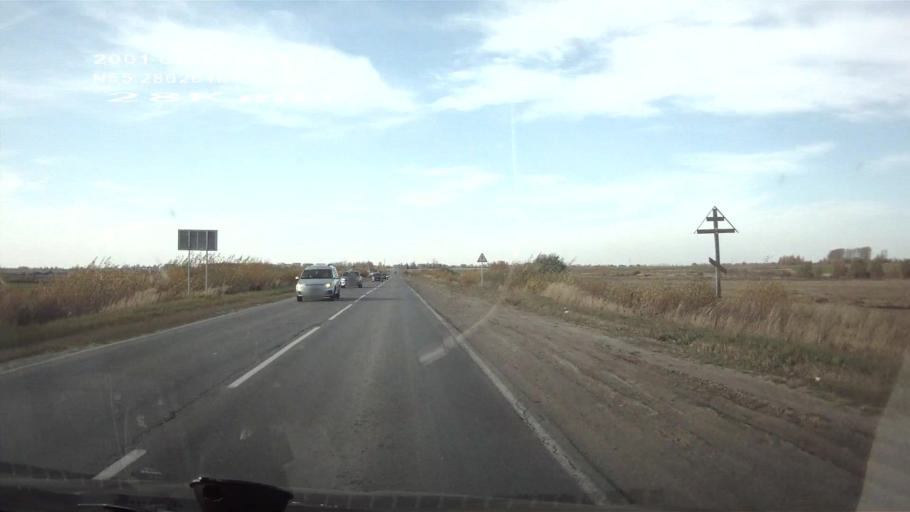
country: RU
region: Chuvashia
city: Ibresi
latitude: 55.2863
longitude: 47.0797
